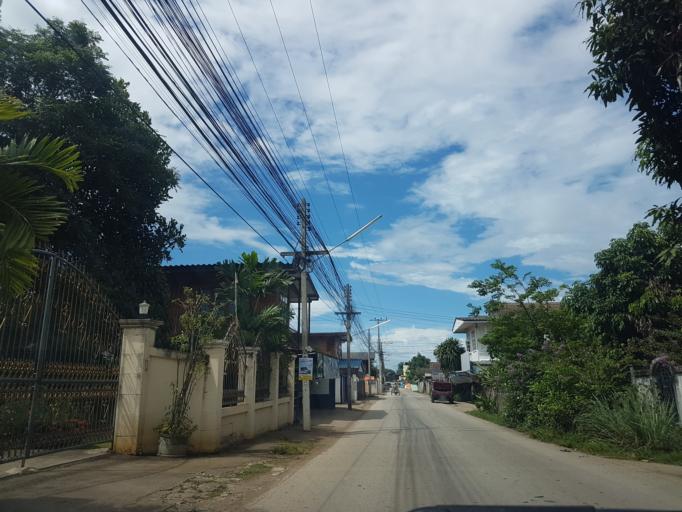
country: TH
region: Lampang
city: Ko Kha
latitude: 18.2403
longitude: 99.4332
